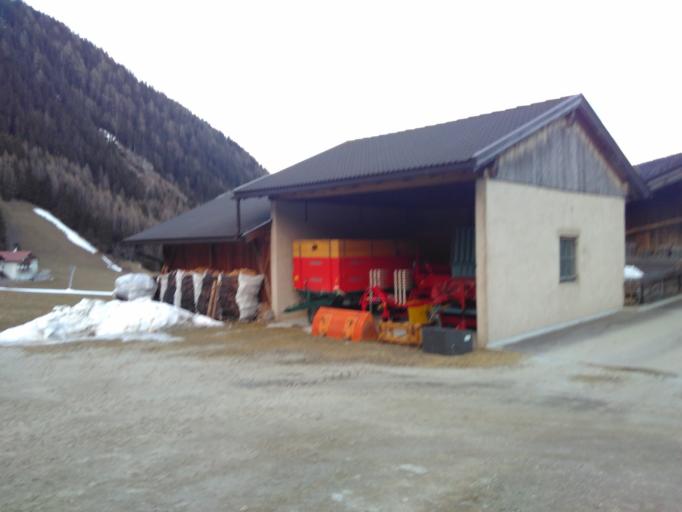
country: IT
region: Trentino-Alto Adige
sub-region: Bolzano
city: Fortezza
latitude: 46.8395
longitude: 11.6281
